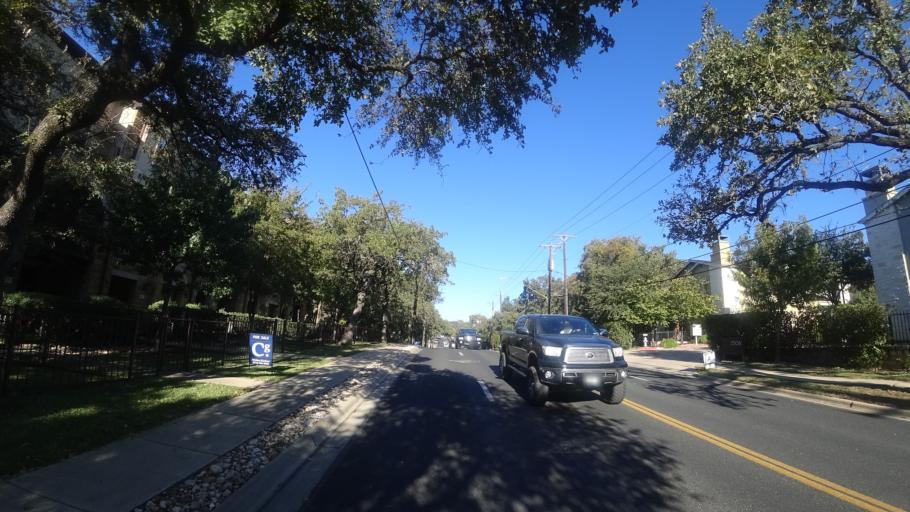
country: US
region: Texas
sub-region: Travis County
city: Rollingwood
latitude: 30.2893
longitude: -97.7700
